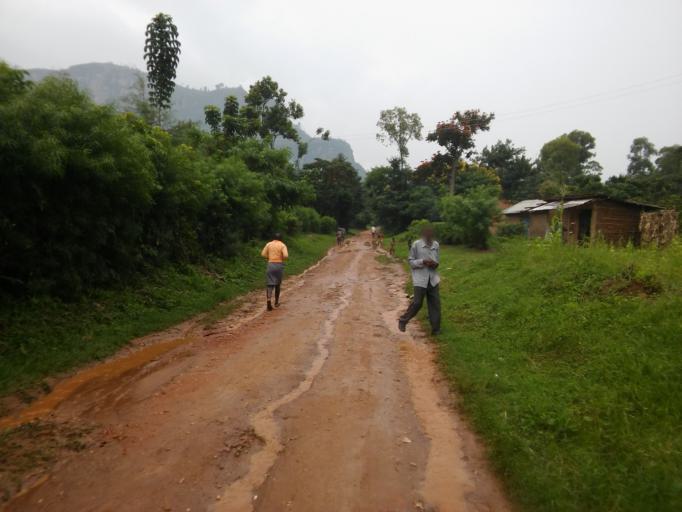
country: UG
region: Eastern Region
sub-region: Bududa District
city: Bududa
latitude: 0.9904
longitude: 34.2305
